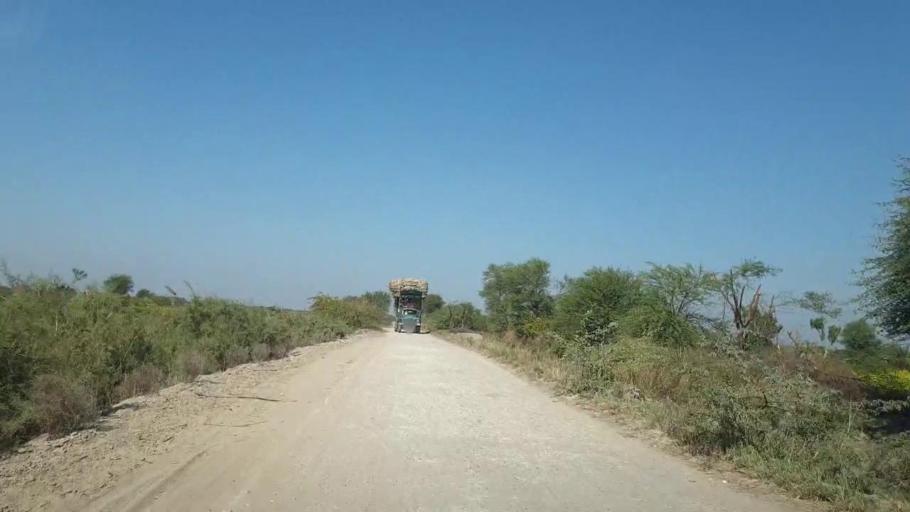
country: PK
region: Sindh
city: Mirpur Khas
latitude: 25.6618
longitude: 69.0269
